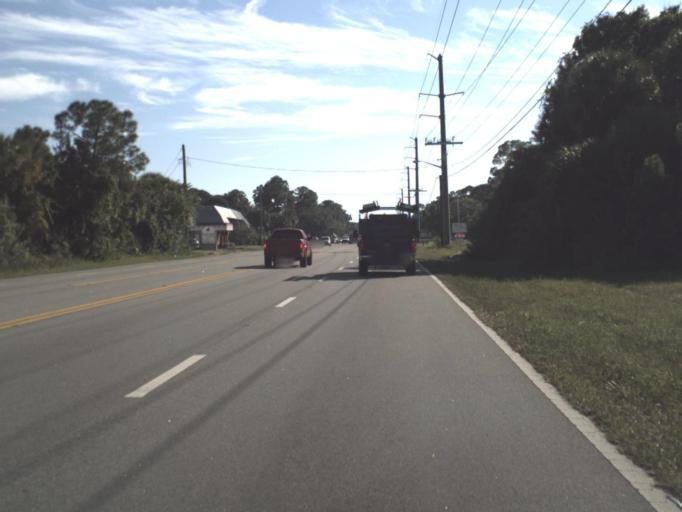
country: US
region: Florida
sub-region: Brevard County
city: June Park
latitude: 28.1079
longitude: -80.6727
